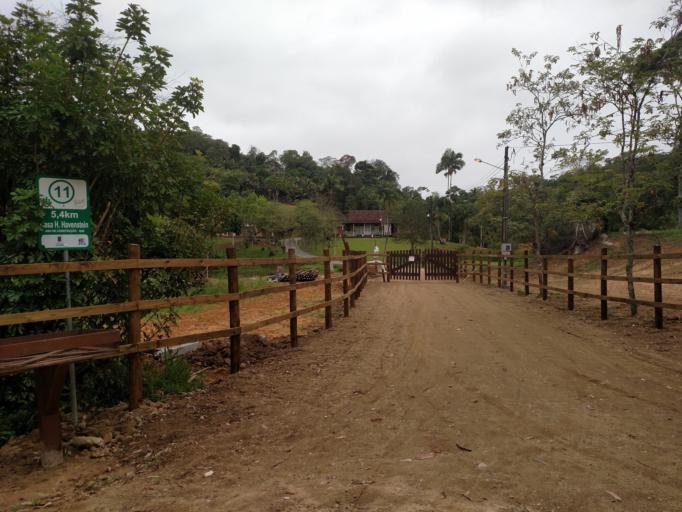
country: BR
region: Santa Catarina
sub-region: Pomerode
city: Pomerode
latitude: -26.7274
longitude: -49.0888
